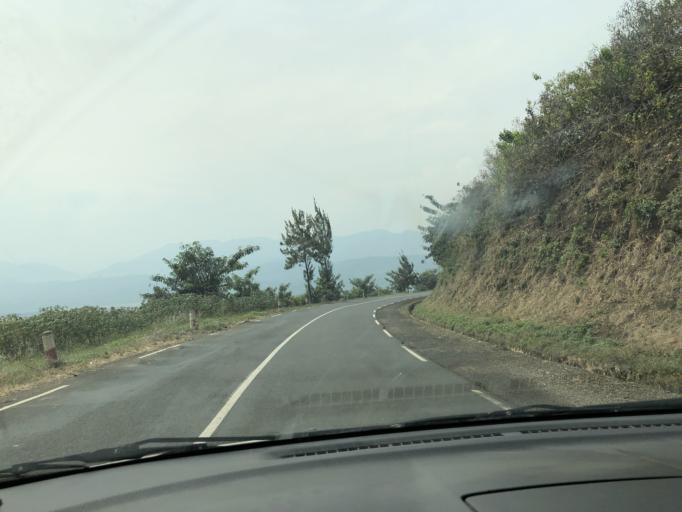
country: RW
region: Western Province
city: Cyangugu
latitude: -2.6672
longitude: 28.9992
